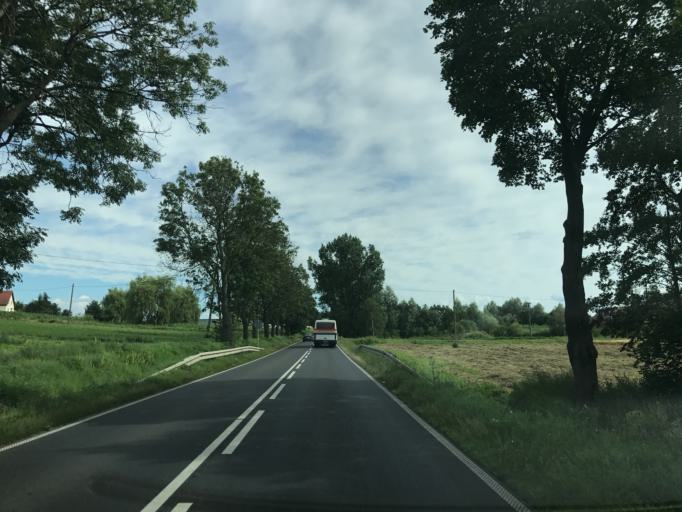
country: PL
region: Kujawsko-Pomorskie
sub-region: Powiat rypinski
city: Rypin
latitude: 53.1041
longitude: 19.3925
